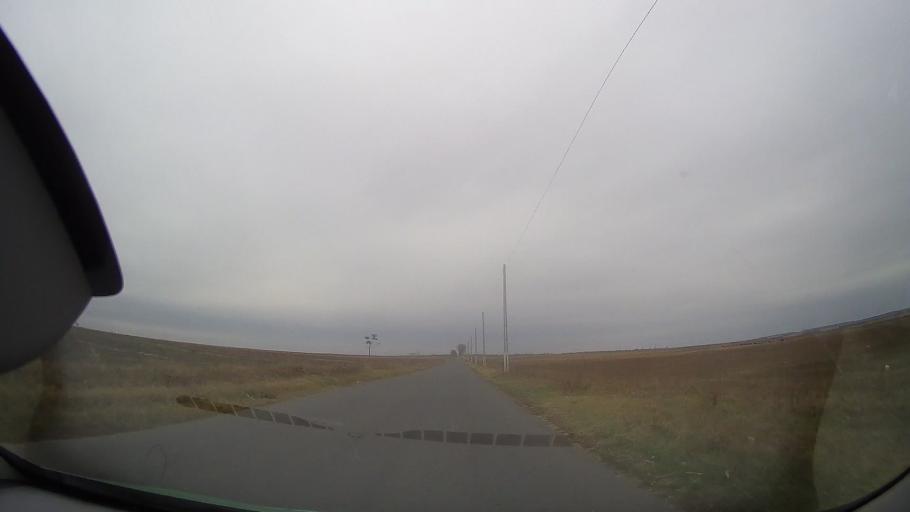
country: RO
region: Braila
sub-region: Comuna Budesti
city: Tataru
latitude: 44.8578
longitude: 27.4236
